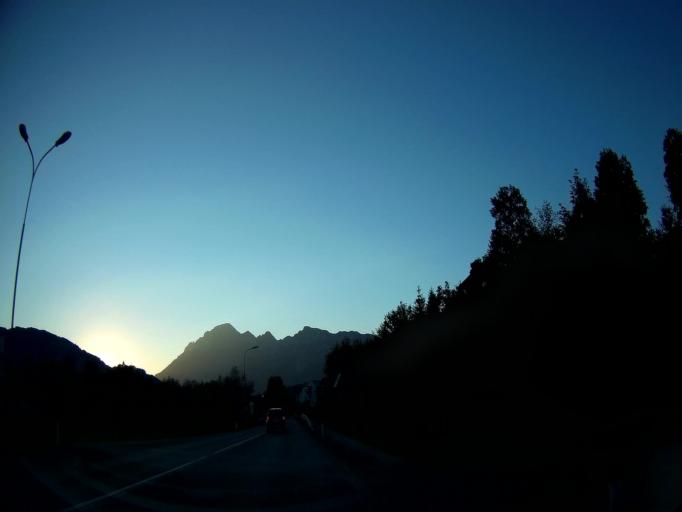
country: AT
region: Salzburg
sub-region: Politischer Bezirk Zell am See
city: Saalfelden am Steinernen Meer
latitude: 47.4164
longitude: 12.8614
